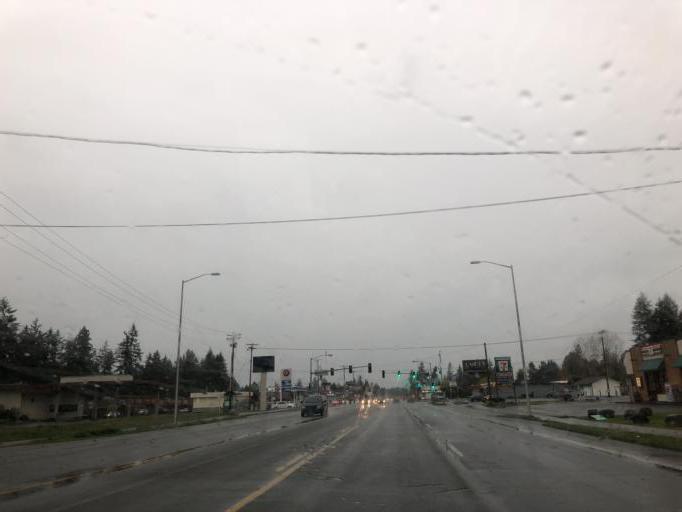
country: US
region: Washington
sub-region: Thurston County
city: Tanglewilde-Thompson Place
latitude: 47.0536
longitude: -122.7810
